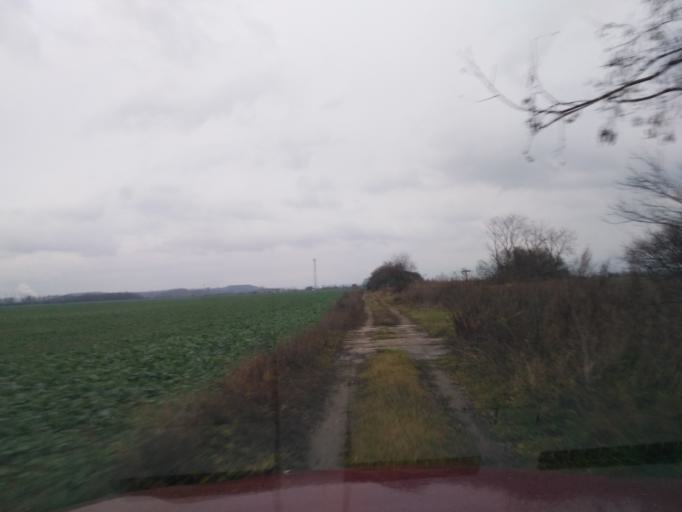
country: SK
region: Kosicky
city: Moldava nad Bodvou
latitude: 48.5620
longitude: 21.1456
